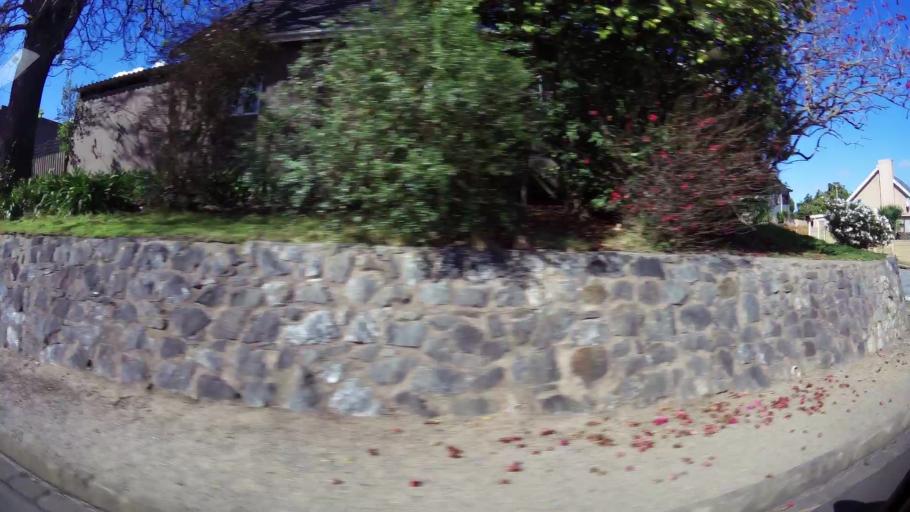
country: ZA
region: Western Cape
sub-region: Eden District Municipality
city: George
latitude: -33.9502
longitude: 22.4713
